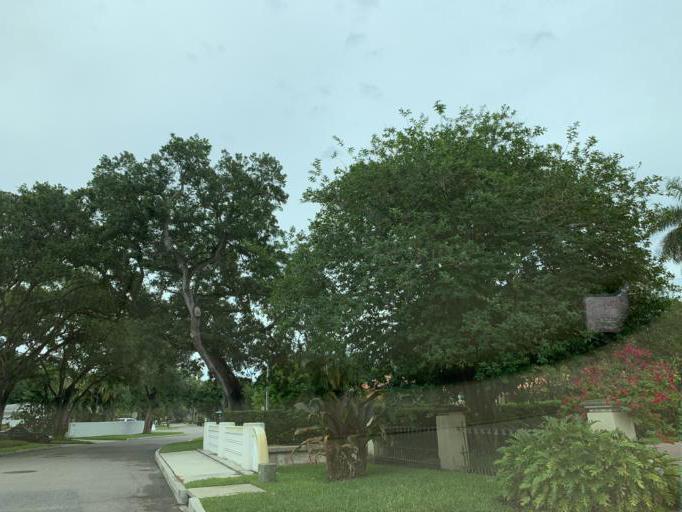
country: US
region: Florida
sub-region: Pinellas County
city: Saint Petersburg
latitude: 27.7941
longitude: -82.6209
